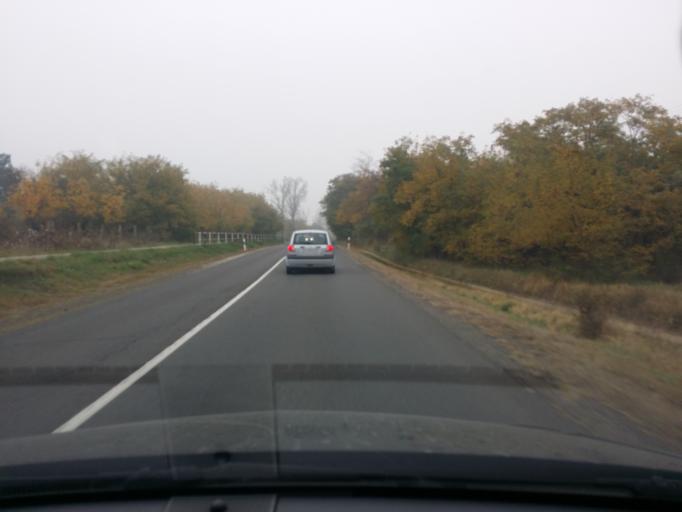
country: HU
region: Szabolcs-Szatmar-Bereg
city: Nyirpazony
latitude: 48.0022
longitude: 21.8197
